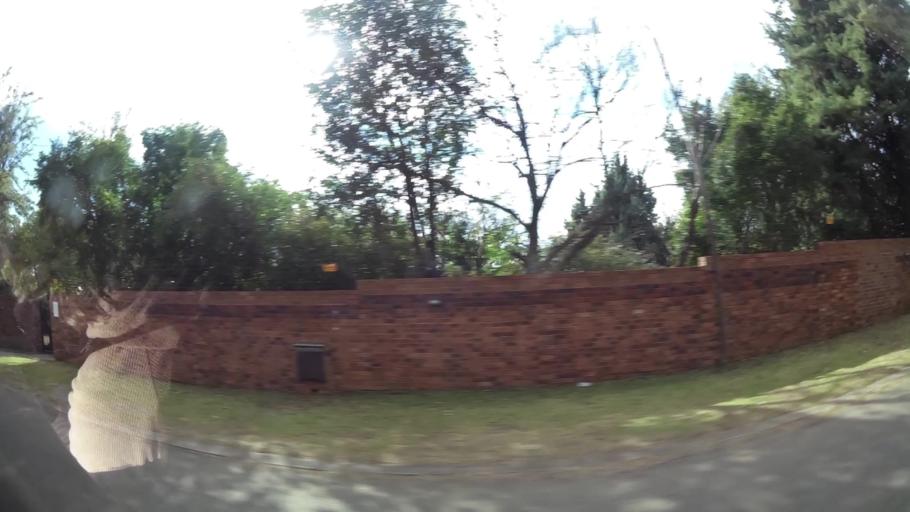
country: ZA
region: Gauteng
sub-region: City of Johannesburg Metropolitan Municipality
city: Roodepoort
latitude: -26.1018
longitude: 27.8715
